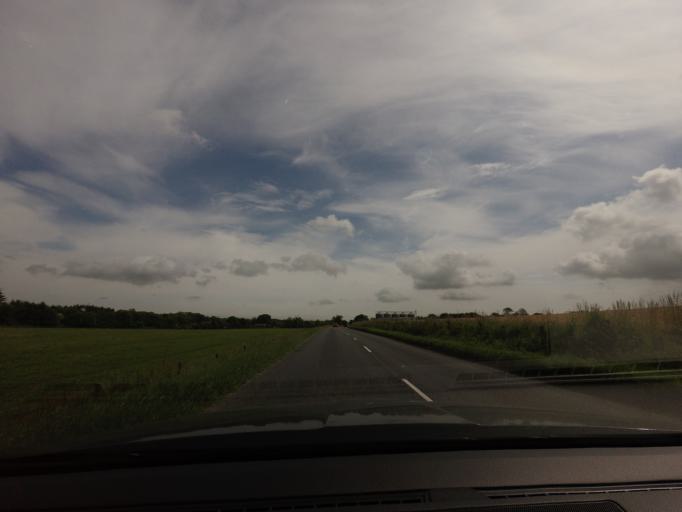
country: GB
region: Scotland
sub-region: Aberdeenshire
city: Mintlaw
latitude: 57.5246
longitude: -1.9873
